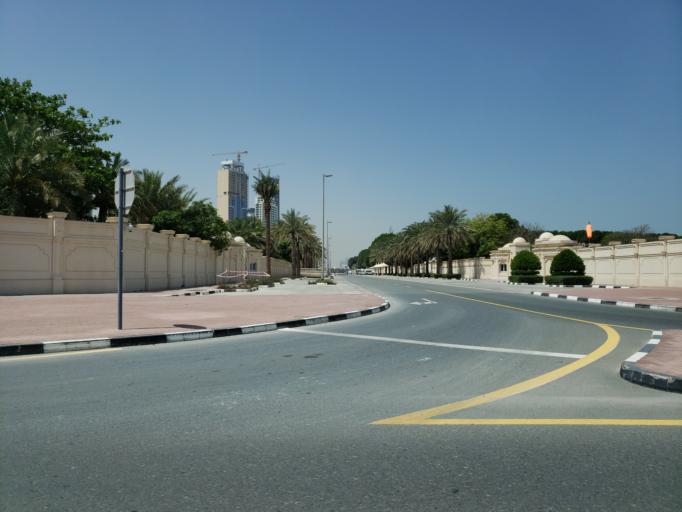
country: AE
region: Dubai
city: Dubai
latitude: 25.1172
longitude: 55.1827
